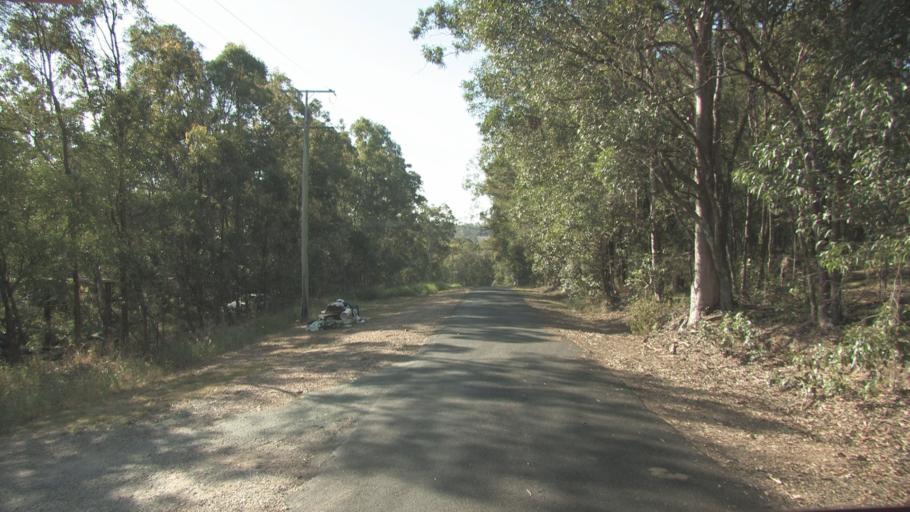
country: AU
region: Queensland
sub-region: Logan
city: Windaroo
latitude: -27.7420
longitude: 153.1649
